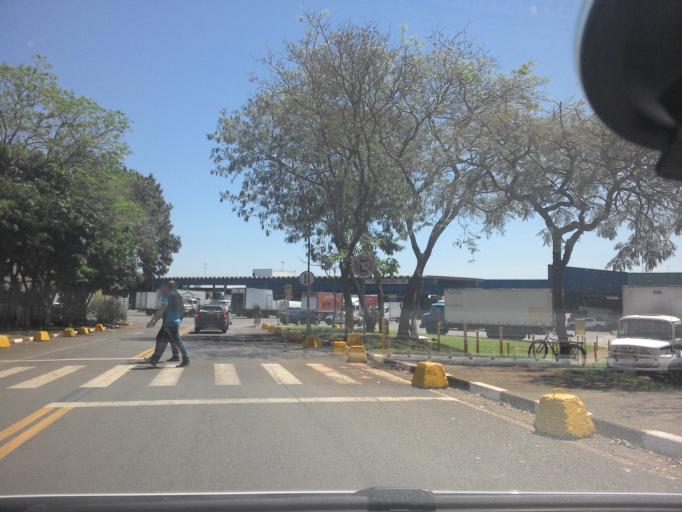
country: BR
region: Sao Paulo
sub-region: Campinas
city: Campinas
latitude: -22.8462
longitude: -47.0941
